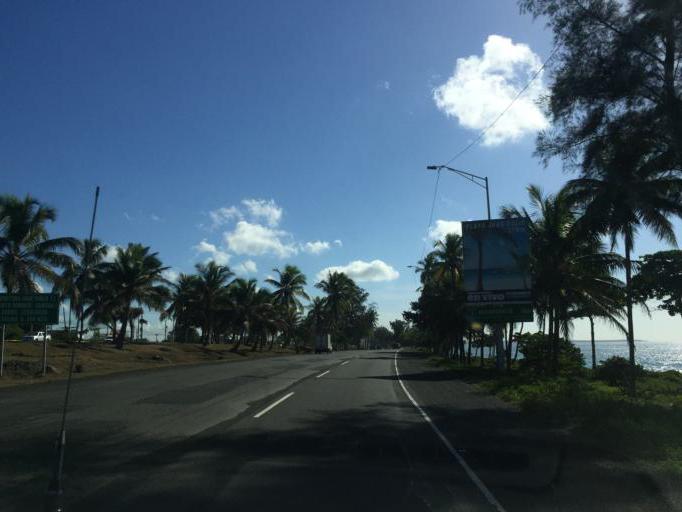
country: DO
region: Santo Domingo
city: Guerra
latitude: 18.4607
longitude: -69.7307
